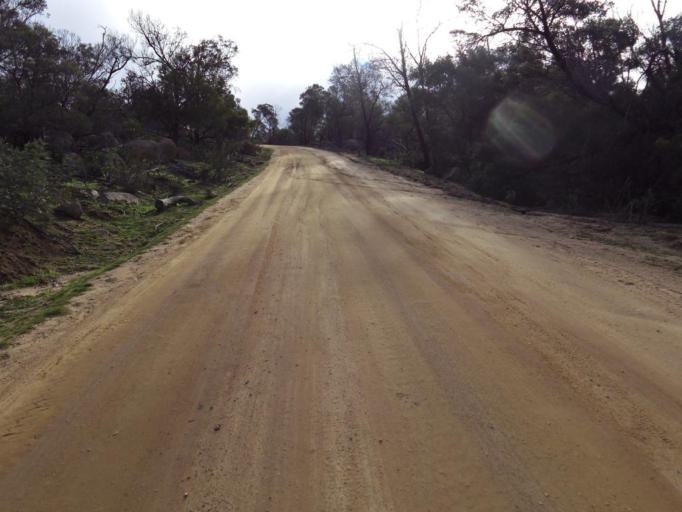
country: AU
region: Victoria
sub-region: Wyndham
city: Little River
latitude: -37.9358
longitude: 144.4382
